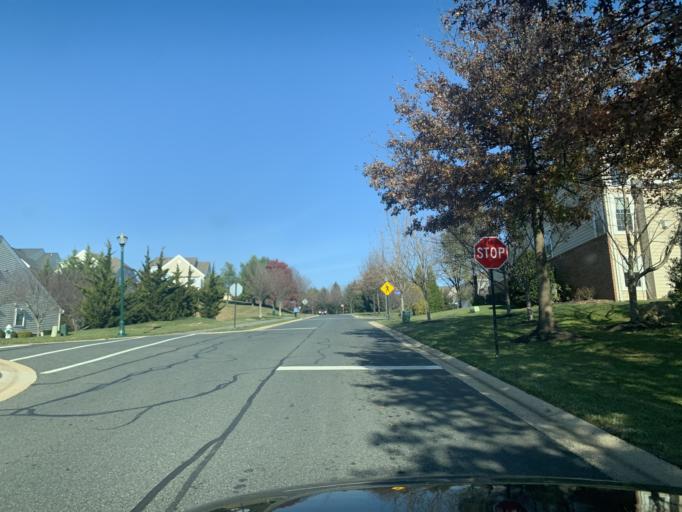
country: US
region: Maryland
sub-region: Harford County
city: Havre de Grace
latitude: 39.5461
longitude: -76.1261
